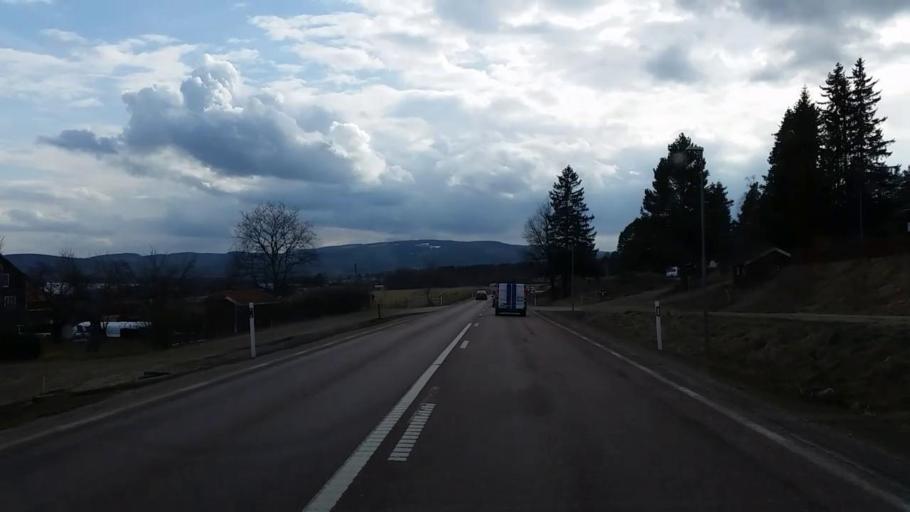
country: SE
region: Gaevleborg
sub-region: Ljusdals Kommun
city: Jaervsoe
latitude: 61.6992
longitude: 16.1627
